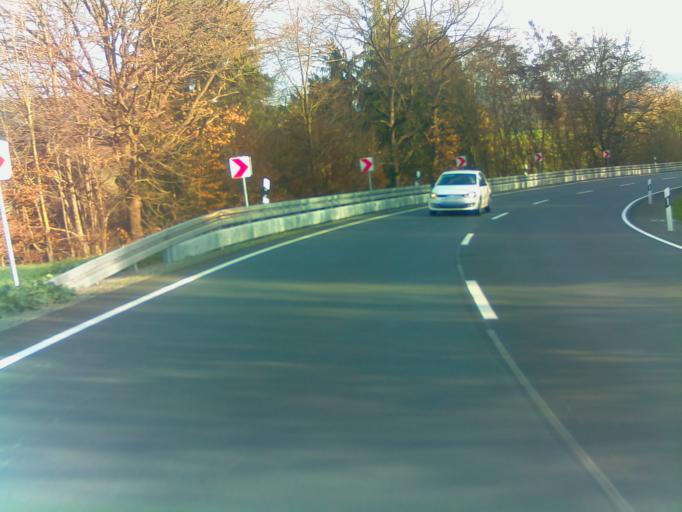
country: DE
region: Bavaria
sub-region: Regierungsbezirk Unterfranken
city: Hammelburg
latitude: 50.1150
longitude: 9.8608
